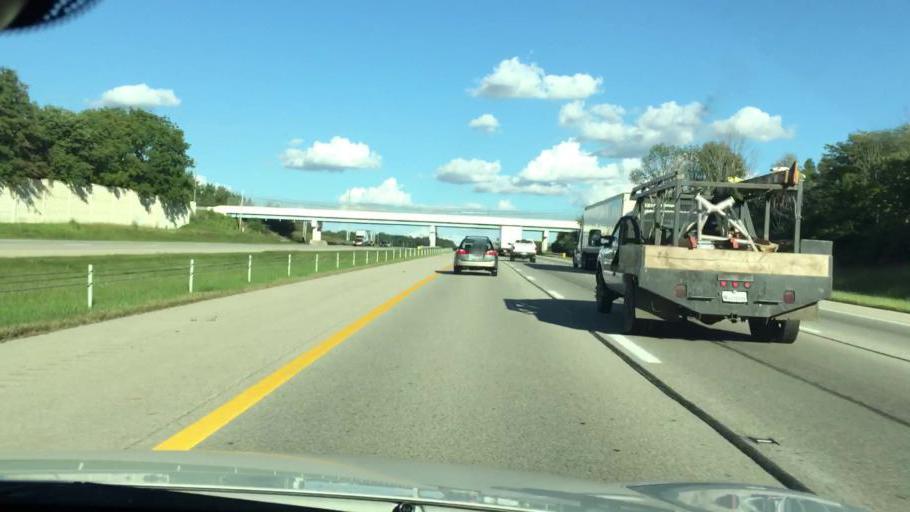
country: US
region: Ohio
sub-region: Clark County
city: Lisbon
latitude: 39.9347
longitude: -83.6488
